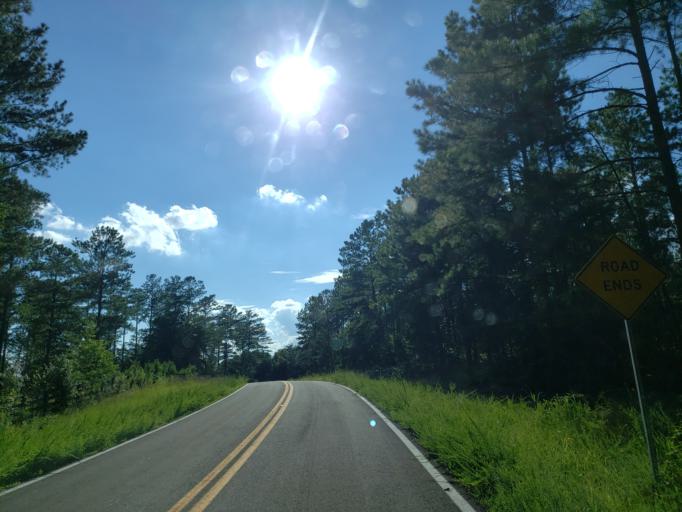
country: US
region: Georgia
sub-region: Bartow County
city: Rydal
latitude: 34.3755
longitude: -84.6332
